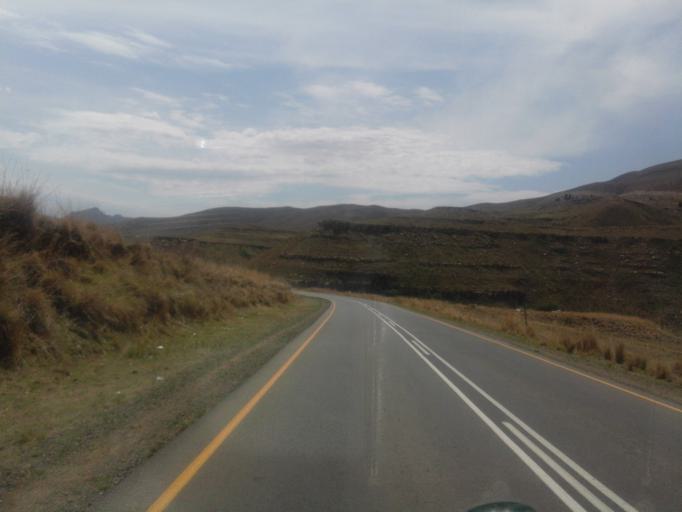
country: LS
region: Qacha's Nek
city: Qacha's Nek
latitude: -30.0998
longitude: 28.6559
